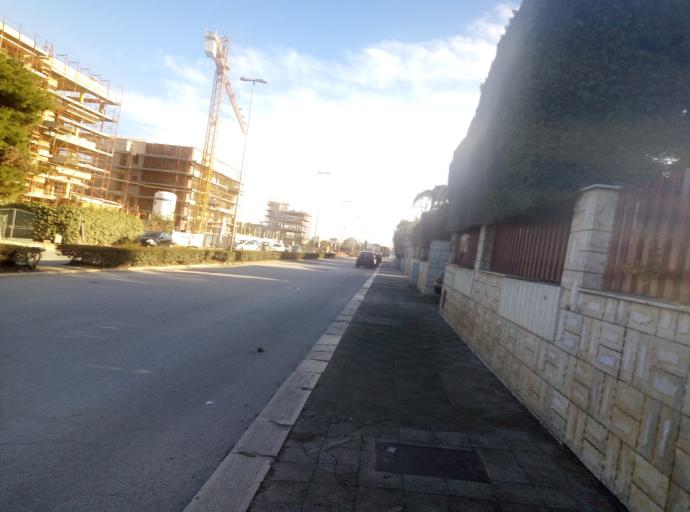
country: IT
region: Apulia
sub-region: Provincia di Bari
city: Ruvo di Puglia
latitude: 41.1207
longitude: 16.4908
